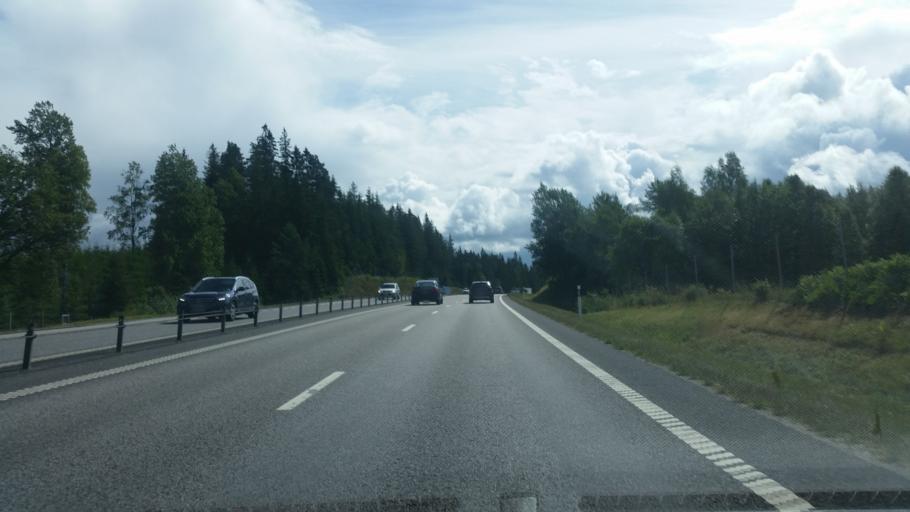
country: SE
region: Joenkoeping
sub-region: Mullsjo Kommun
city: Mullsjoe
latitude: 57.7711
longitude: 13.7133
